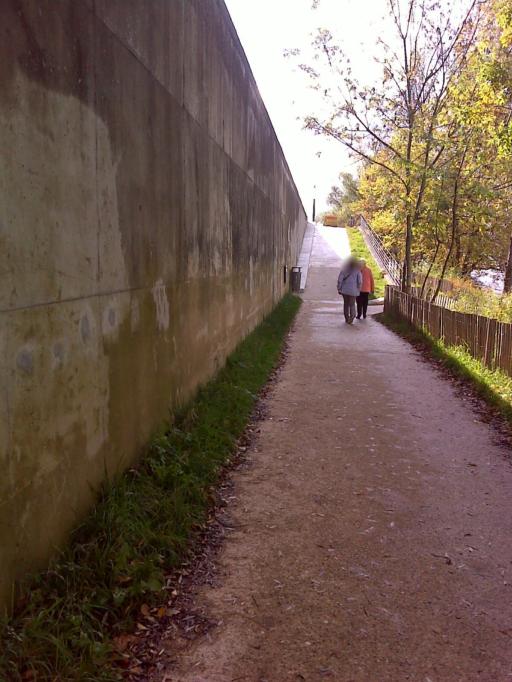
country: FR
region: Rhone-Alpes
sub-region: Departement du Rhone
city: Caluire-et-Cuire
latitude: 45.7846
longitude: 4.8153
